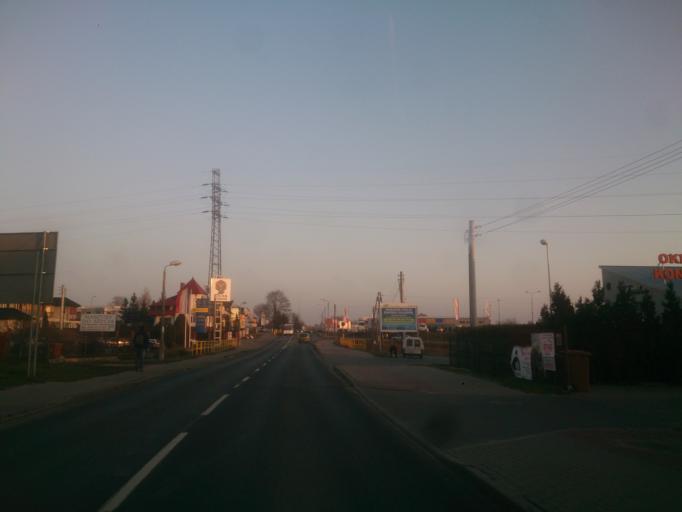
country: PL
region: Kujawsko-Pomorskie
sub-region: Powiat brodnicki
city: Brodnica
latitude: 53.2361
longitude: 19.3912
